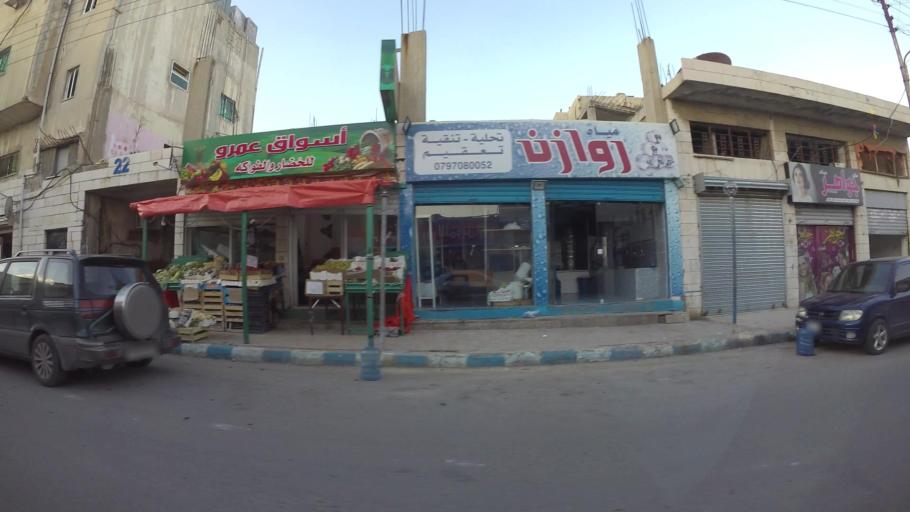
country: JO
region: Amman
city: Al Bunayyat ash Shamaliyah
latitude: 31.9060
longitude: 35.9093
